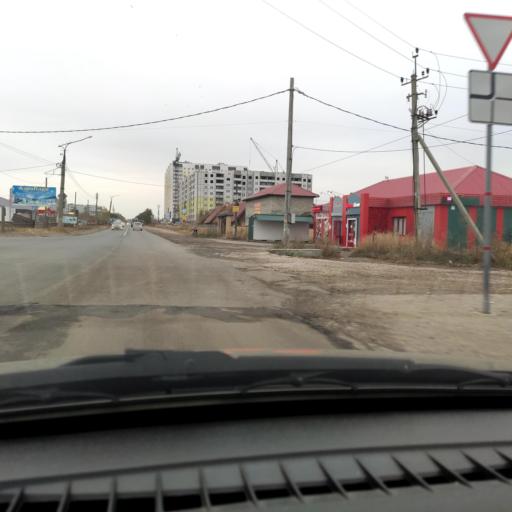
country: RU
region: Samara
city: Tol'yatti
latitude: 53.5095
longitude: 49.2443
